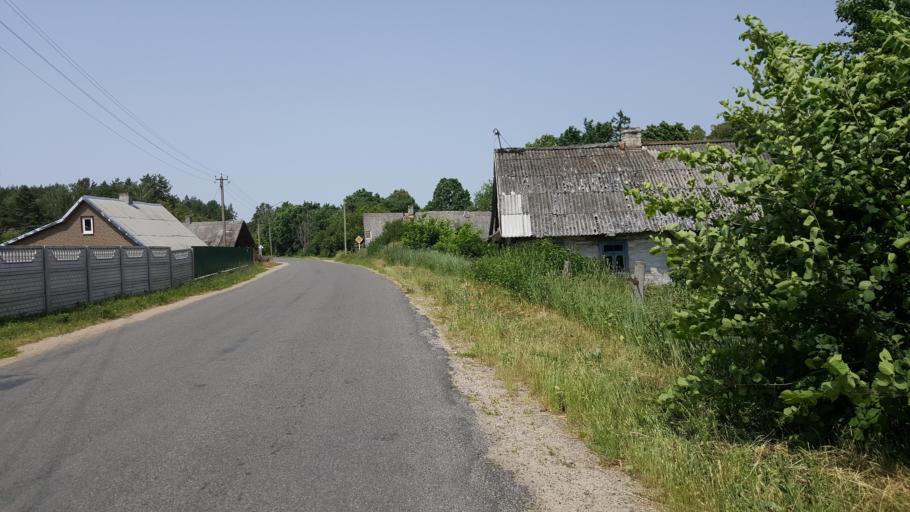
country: BY
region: Brest
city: Kamyanyuki
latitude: 52.4977
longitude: 23.8679
